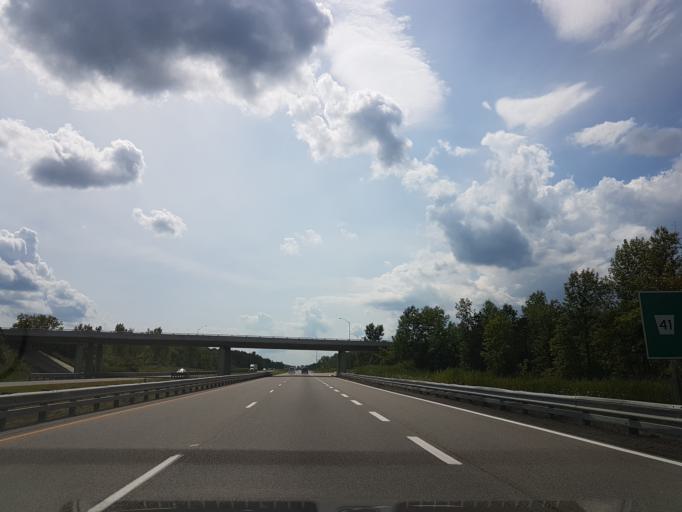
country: US
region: New York
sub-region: St. Lawrence County
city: Norfolk
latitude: 44.9539
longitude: -75.1085
